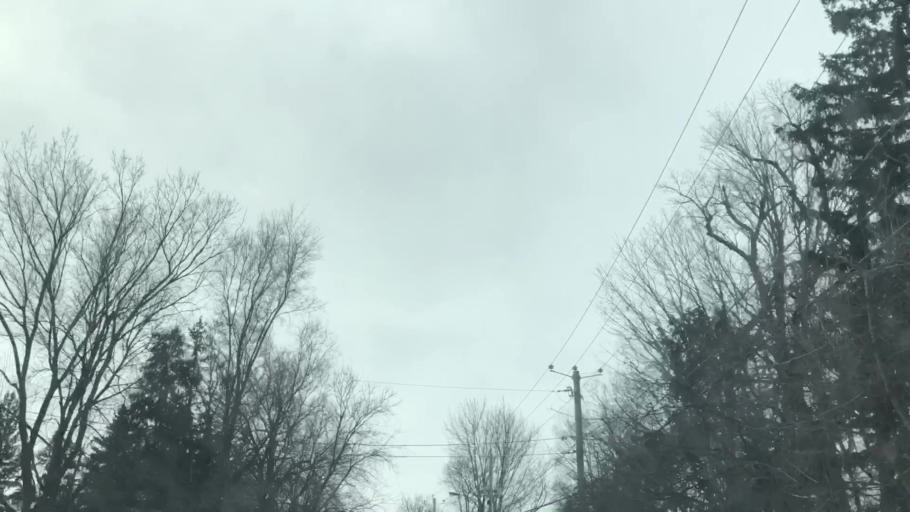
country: CA
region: Quebec
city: Dorval
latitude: 45.5128
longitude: -73.7494
